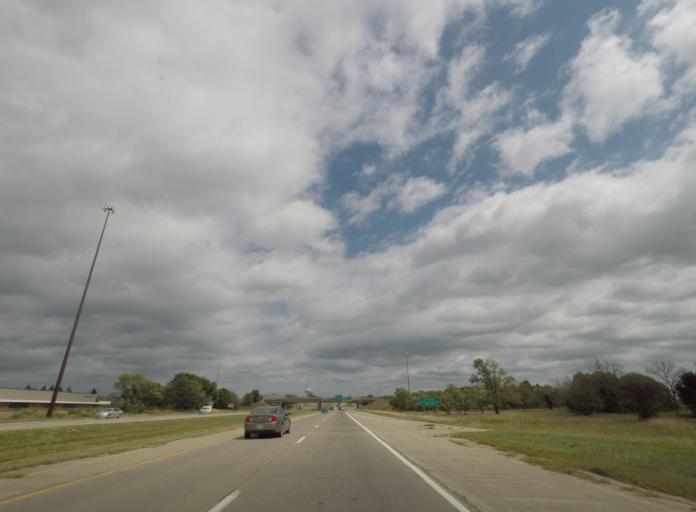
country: US
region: Iowa
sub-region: Linn County
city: Cedar Rapids
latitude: 41.9268
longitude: -91.6603
